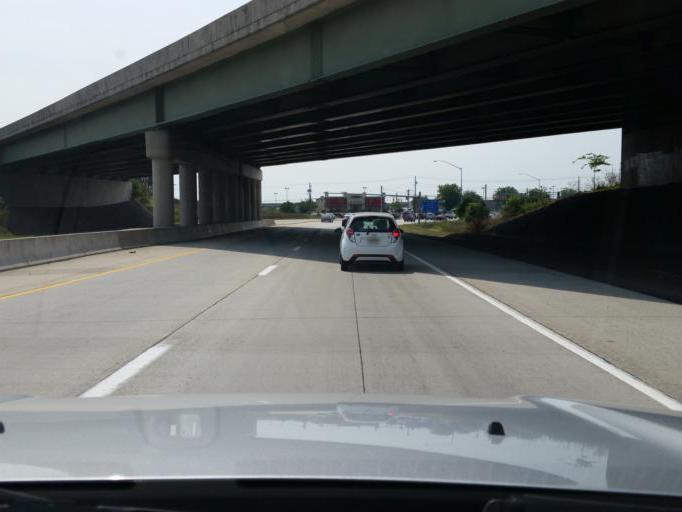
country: US
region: Pennsylvania
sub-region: Cumberland County
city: Shiremanstown
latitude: 40.2408
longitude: -76.9790
